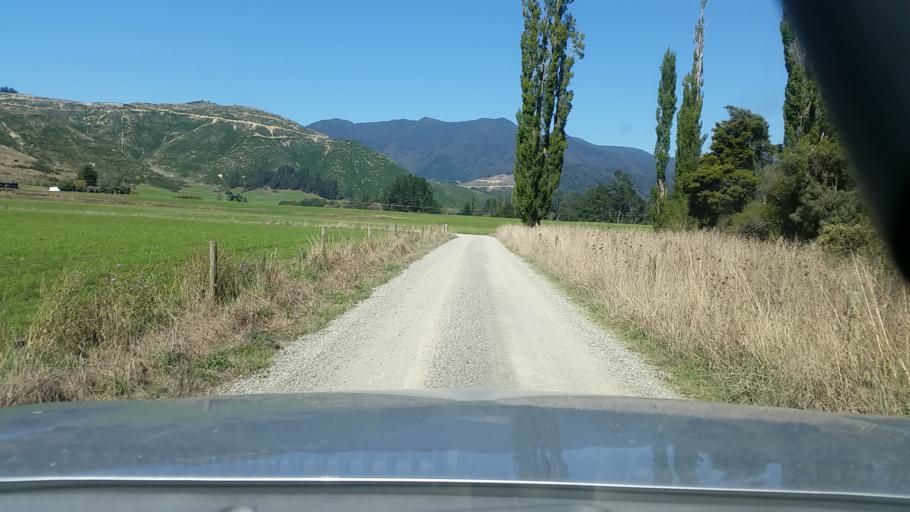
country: NZ
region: Nelson
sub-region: Nelson City
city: Nelson
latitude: -41.2687
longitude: 173.5755
